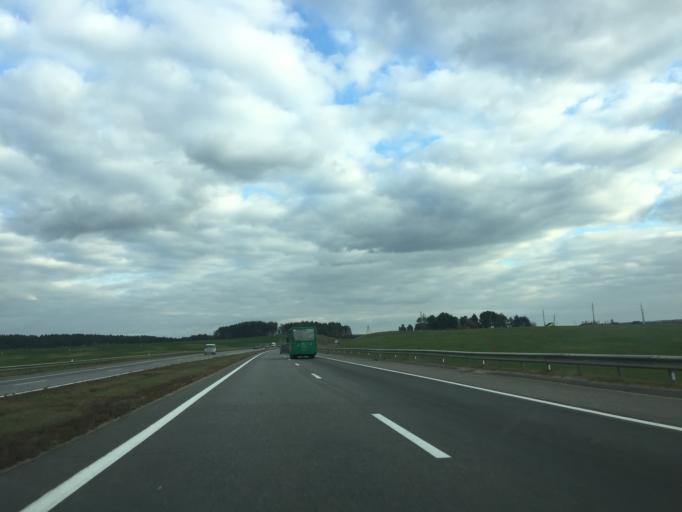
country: BY
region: Minsk
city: Rakaw
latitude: 53.9754
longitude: 27.0678
